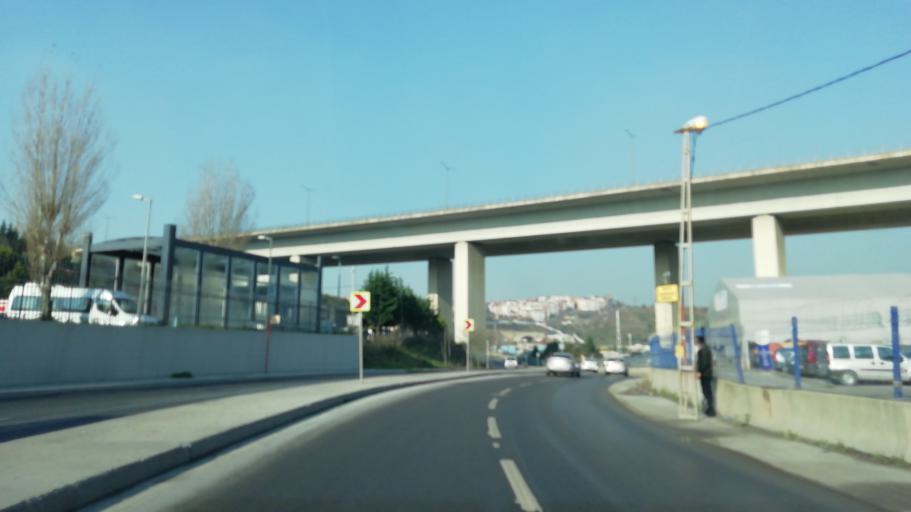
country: TR
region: Istanbul
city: Sultangazi
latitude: 41.0934
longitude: 28.9222
